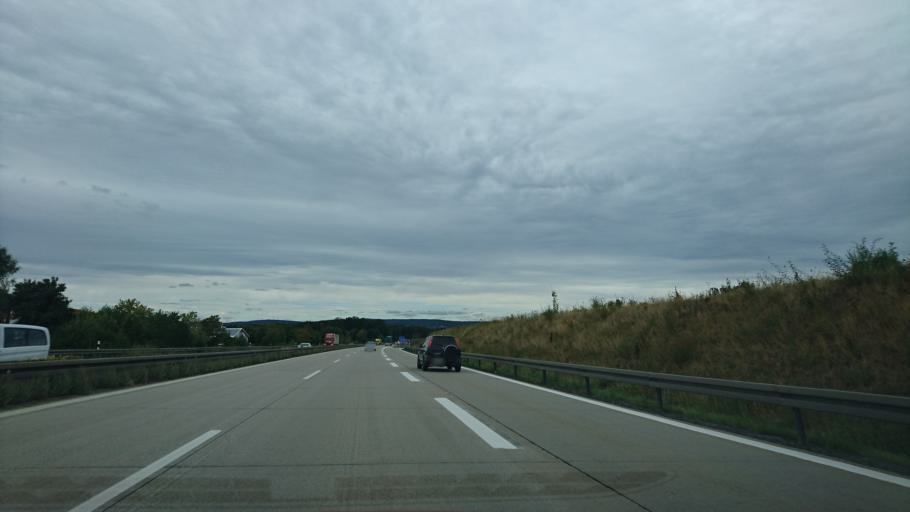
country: DE
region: Bavaria
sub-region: Upper Palatinate
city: Wernberg-Koblitz
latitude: 49.5306
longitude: 12.1437
